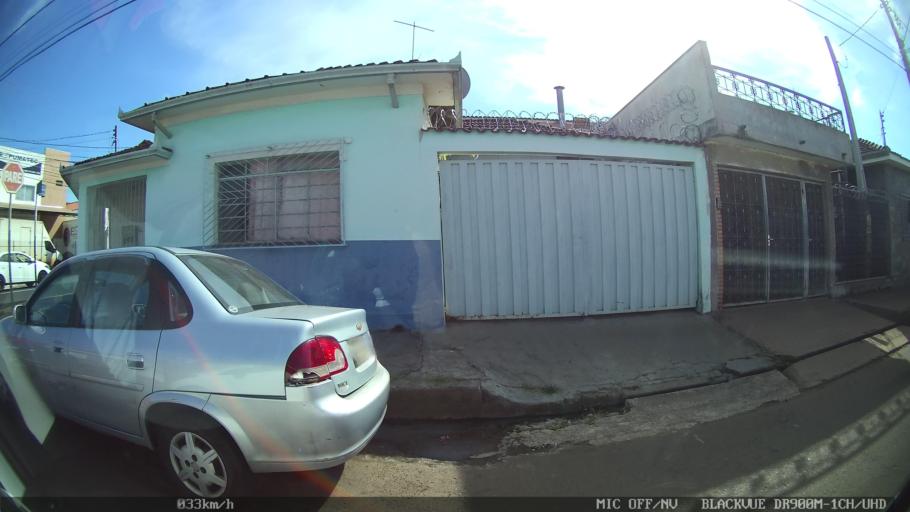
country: BR
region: Sao Paulo
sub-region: Franca
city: Franca
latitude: -20.5335
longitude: -47.4145
